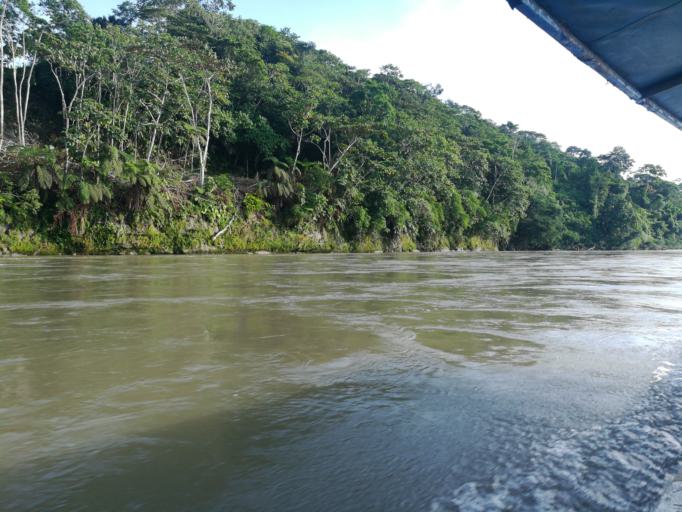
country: EC
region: Orellana
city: Boca Suno
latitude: -0.8637
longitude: -77.2486
